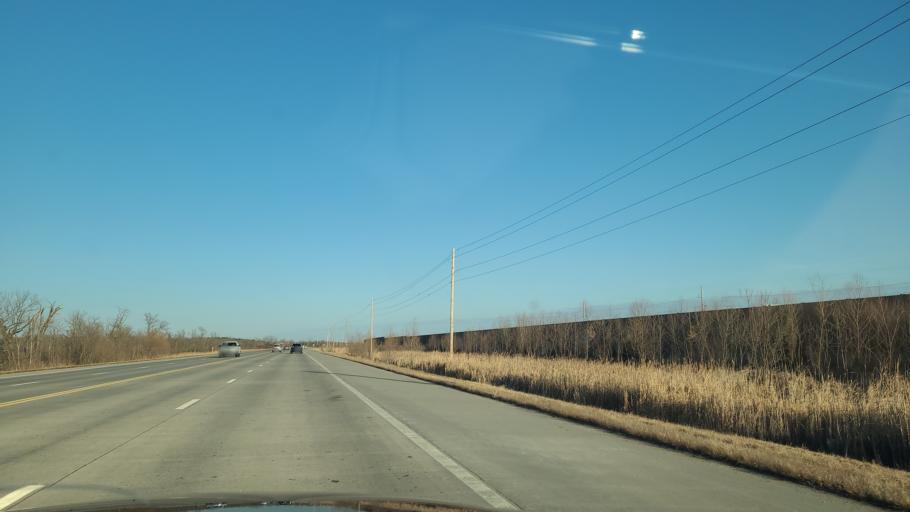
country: US
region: Kansas
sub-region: Douglas County
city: Lawrence
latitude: 38.9270
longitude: -95.2348
